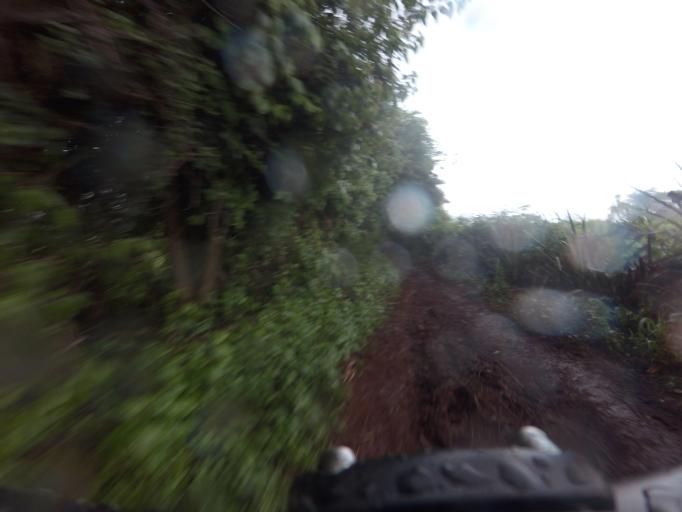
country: CU
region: Pinar del Rio
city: Vinales
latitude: 22.6177
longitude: -83.7160
